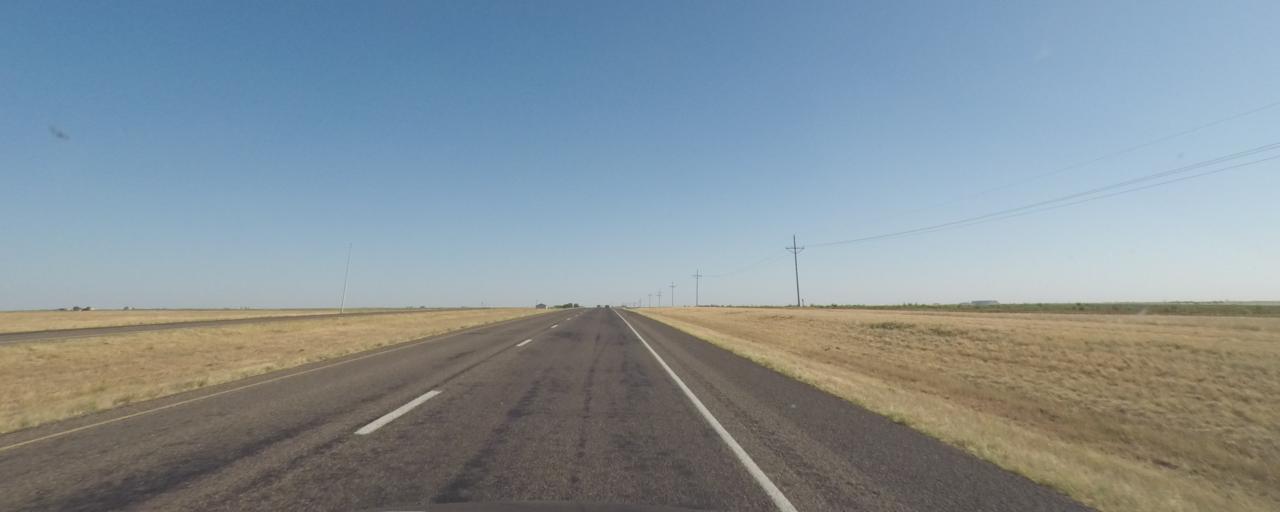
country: US
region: Texas
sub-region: Gaines County
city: Seagraves
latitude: 32.8589
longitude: -102.6402
